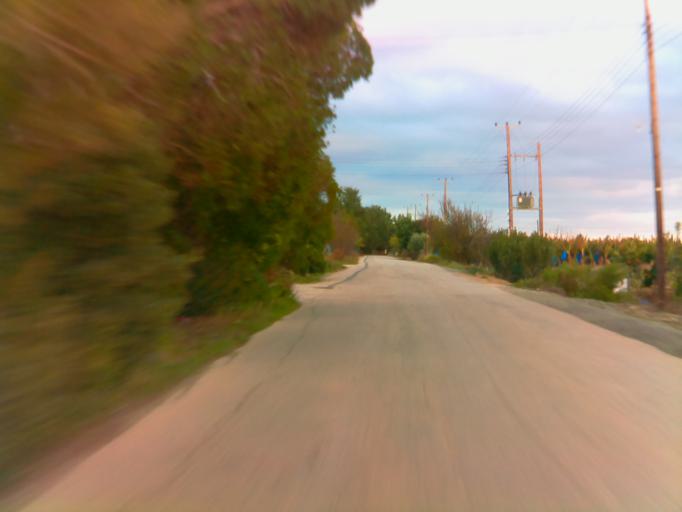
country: CY
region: Pafos
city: Pegeia
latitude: 34.8652
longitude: 32.3525
